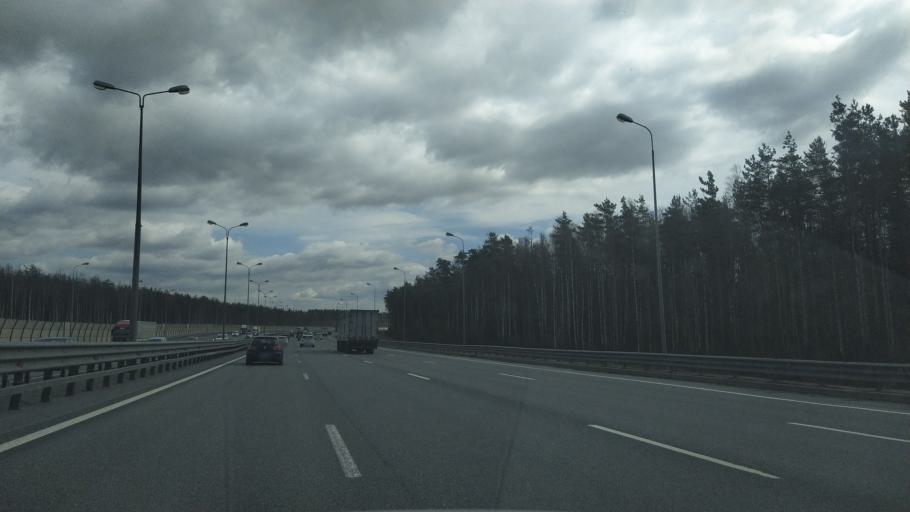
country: RU
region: St.-Petersburg
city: Krasnogvargeisky
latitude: 59.9751
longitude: 30.5386
